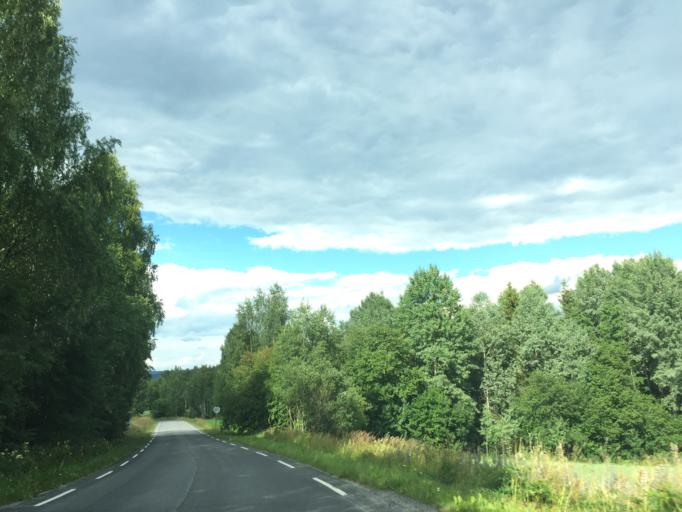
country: NO
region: Hedmark
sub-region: Kongsvinger
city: Spetalen
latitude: 60.1987
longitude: 11.8396
